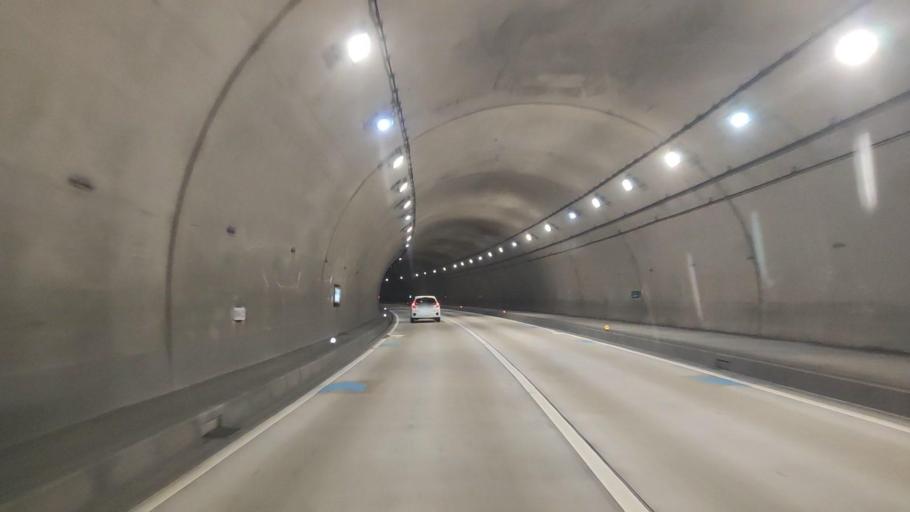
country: JP
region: Wakayama
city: Shingu
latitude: 33.7403
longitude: 135.9930
